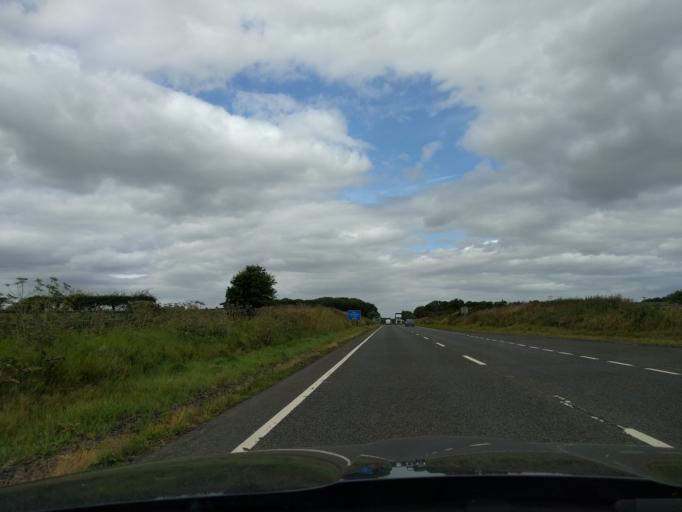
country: GB
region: England
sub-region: Northumberland
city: Ellingham
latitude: 55.4707
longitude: -1.7163
